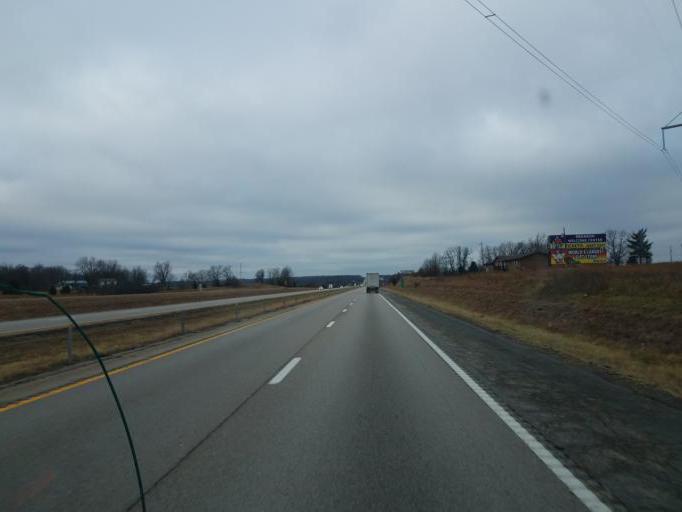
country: US
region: Missouri
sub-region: Laclede County
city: Lebanon
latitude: 37.5814
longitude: -92.7488
